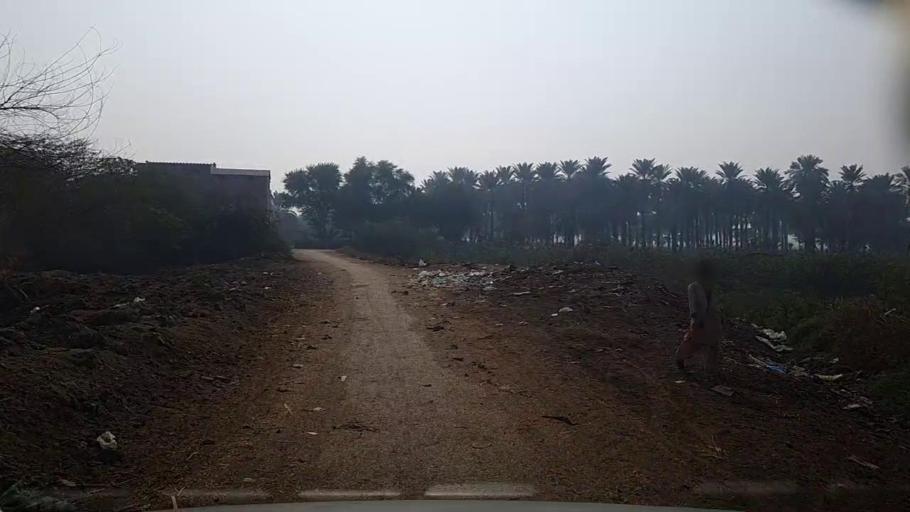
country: PK
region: Sindh
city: Setharja Old
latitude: 27.1585
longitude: 68.4630
